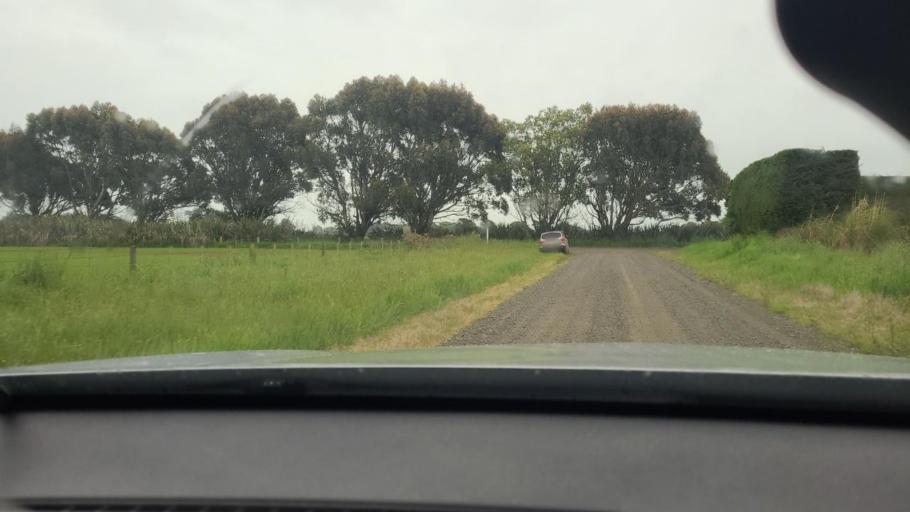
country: NZ
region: Southland
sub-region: Southland District
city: Riverton
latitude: -46.3049
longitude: 168.1451
